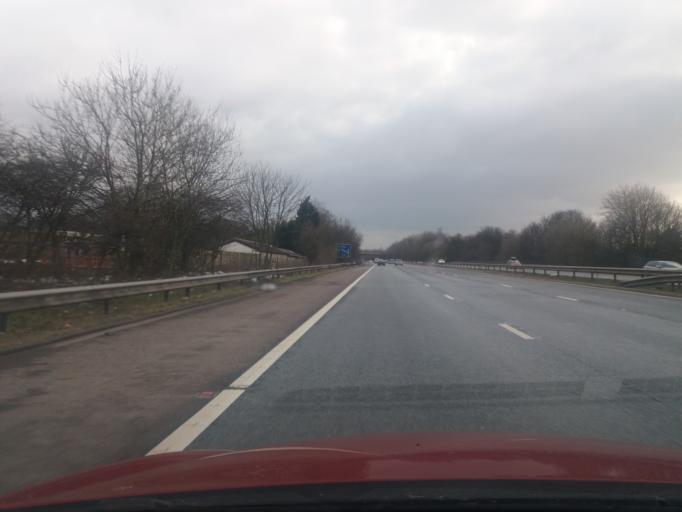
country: GB
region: England
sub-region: Lancashire
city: Chorley
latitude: 53.6846
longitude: -2.6256
